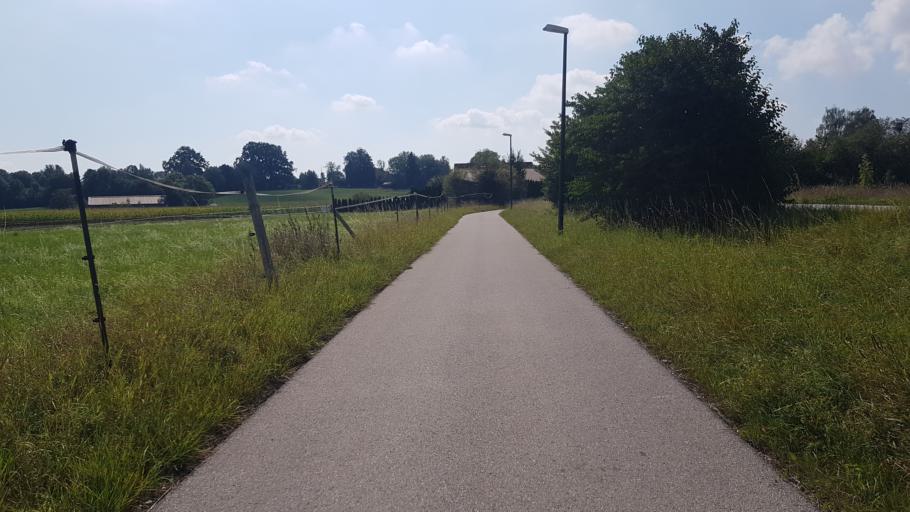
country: DE
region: Bavaria
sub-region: Upper Bavaria
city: Wessling
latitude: 48.0798
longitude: 11.2660
